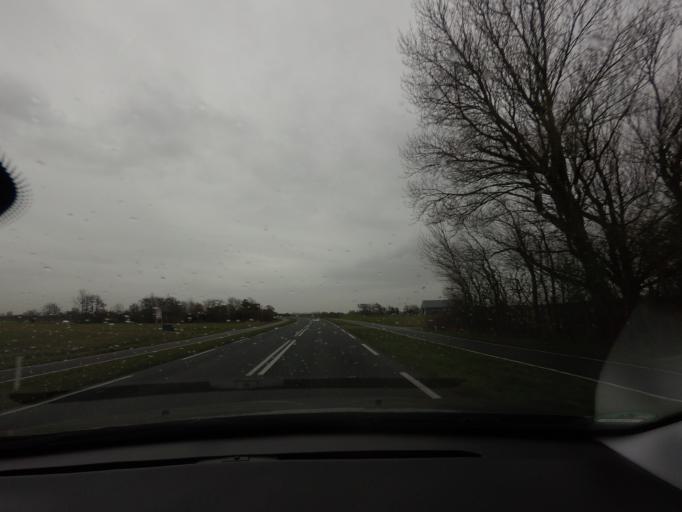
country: NL
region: North Holland
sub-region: Gemeente Texel
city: Den Burg
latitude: 53.0711
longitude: 4.7729
